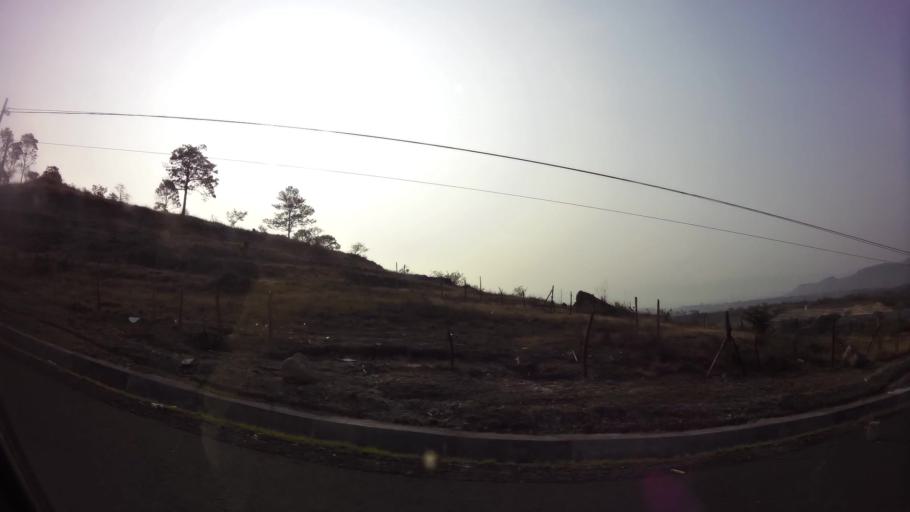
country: HN
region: Francisco Morazan
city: Zambrano
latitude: 14.2352
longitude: -87.3883
